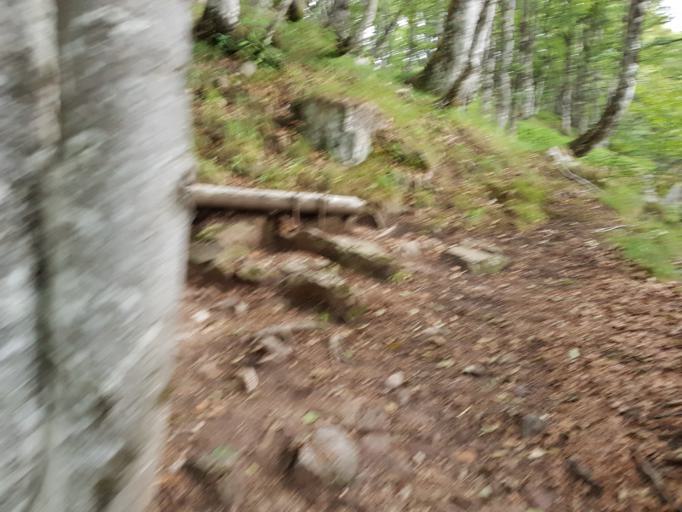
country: FR
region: Alsace
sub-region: Departement du Haut-Rhin
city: Soultzeren
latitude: 48.0905
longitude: 7.0588
